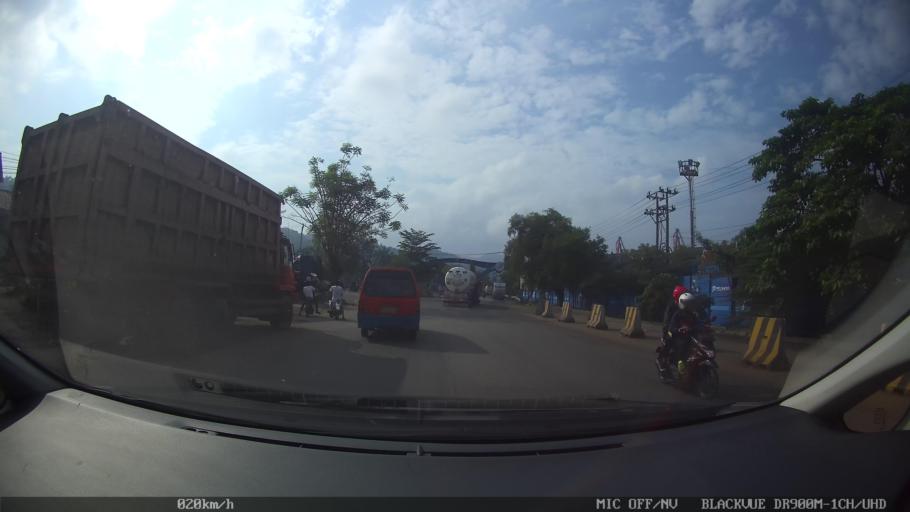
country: ID
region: Lampung
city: Panjang
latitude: -5.4652
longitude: 105.3189
